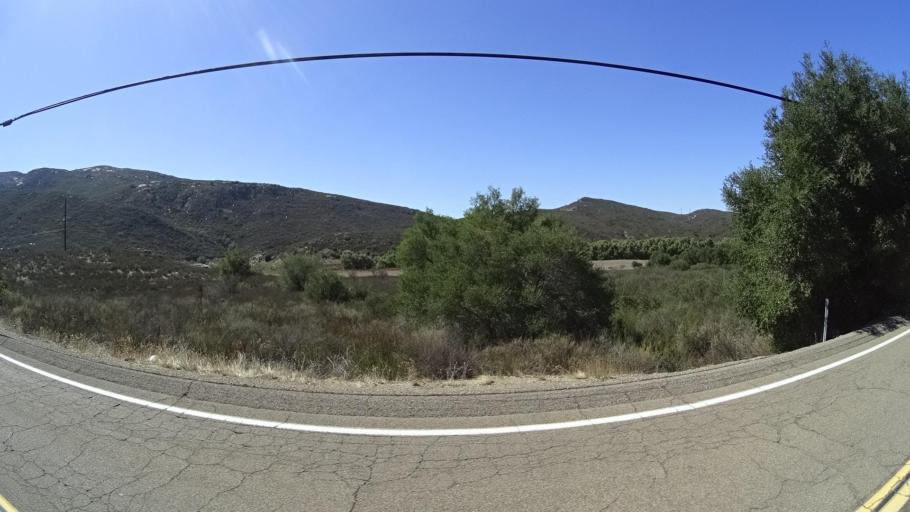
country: US
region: California
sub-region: San Diego County
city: Alpine
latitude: 32.7971
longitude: -116.7468
